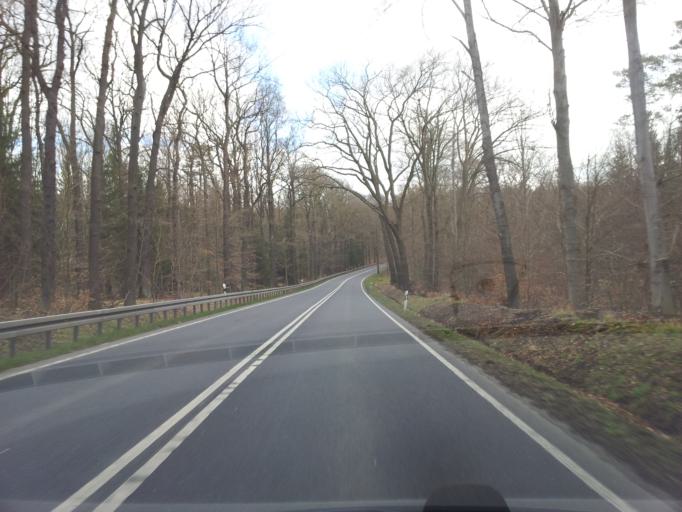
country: DE
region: Saxony
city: Laussnitz
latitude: 51.2354
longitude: 13.8468
